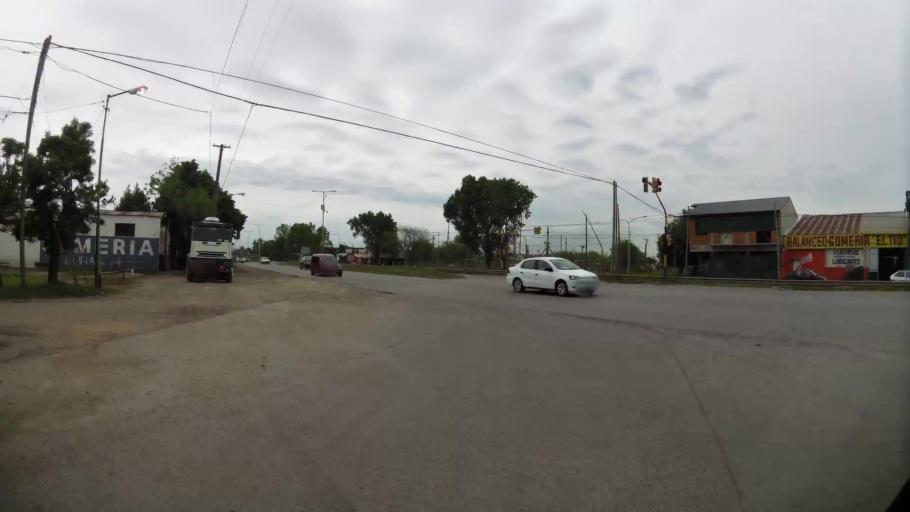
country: AR
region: Buenos Aires
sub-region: Partido de Campana
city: Campana
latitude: -34.1822
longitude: -58.9427
